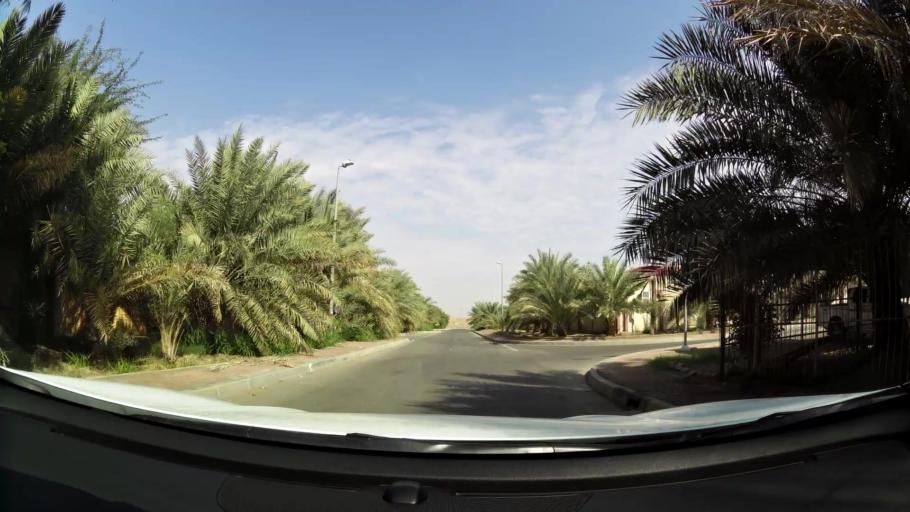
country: AE
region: Abu Dhabi
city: Al Ain
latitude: 24.0984
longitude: 55.9226
